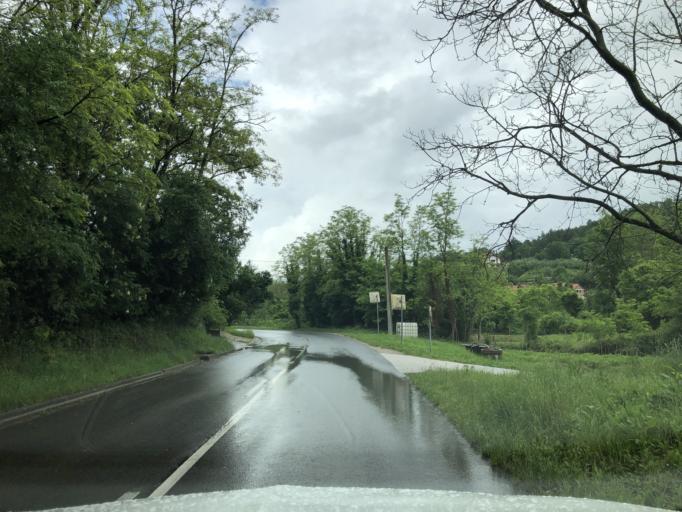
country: SI
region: Koper-Capodistria
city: Prade
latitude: 45.5155
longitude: 13.7800
